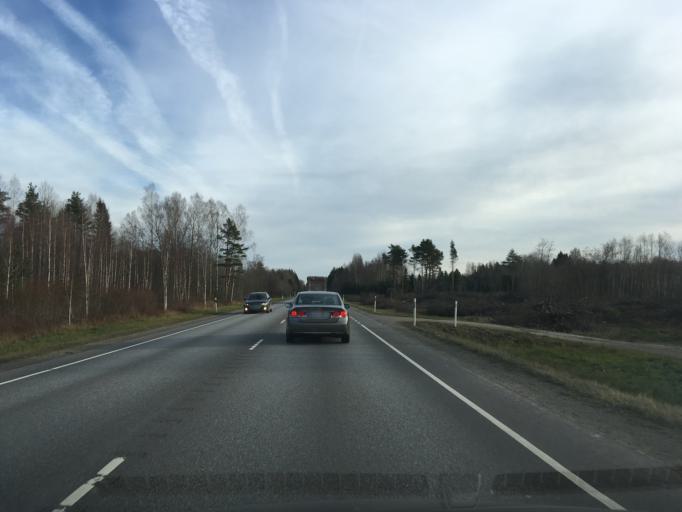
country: EE
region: Ida-Virumaa
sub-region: Toila vald
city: Toila
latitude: 59.3757
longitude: 27.5290
